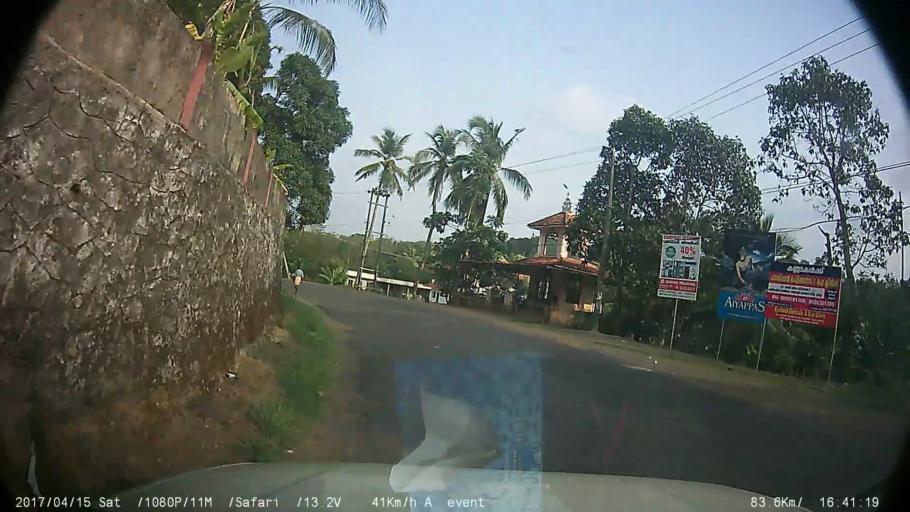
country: IN
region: Kerala
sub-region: Kottayam
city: Kottayam
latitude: 9.6452
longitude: 76.5271
